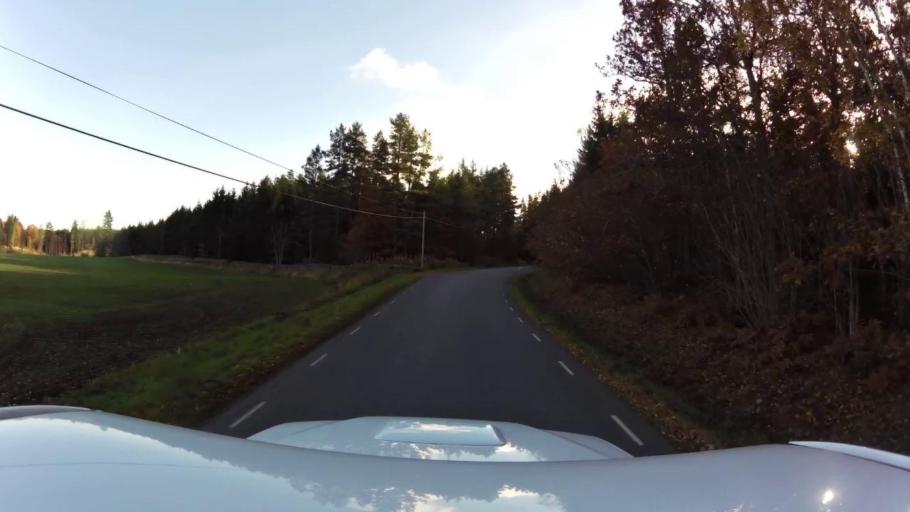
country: SE
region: OEstergoetland
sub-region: Linkopings Kommun
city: Vikingstad
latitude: 58.2720
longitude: 15.4376
